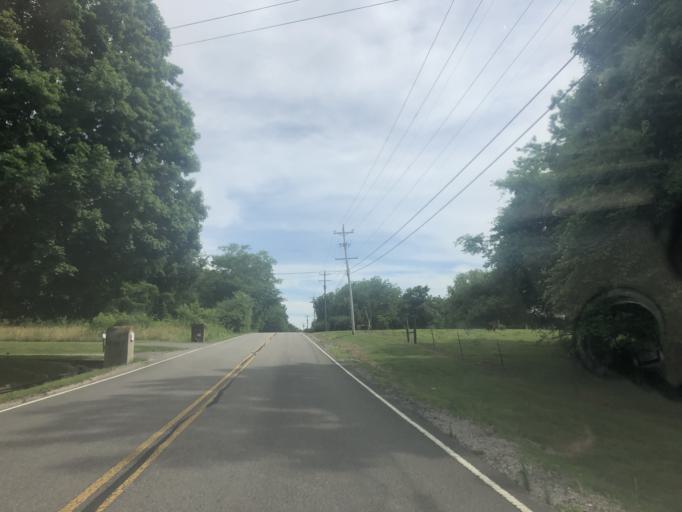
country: US
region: Tennessee
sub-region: Davidson County
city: Lakewood
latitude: 36.2114
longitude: -86.6658
